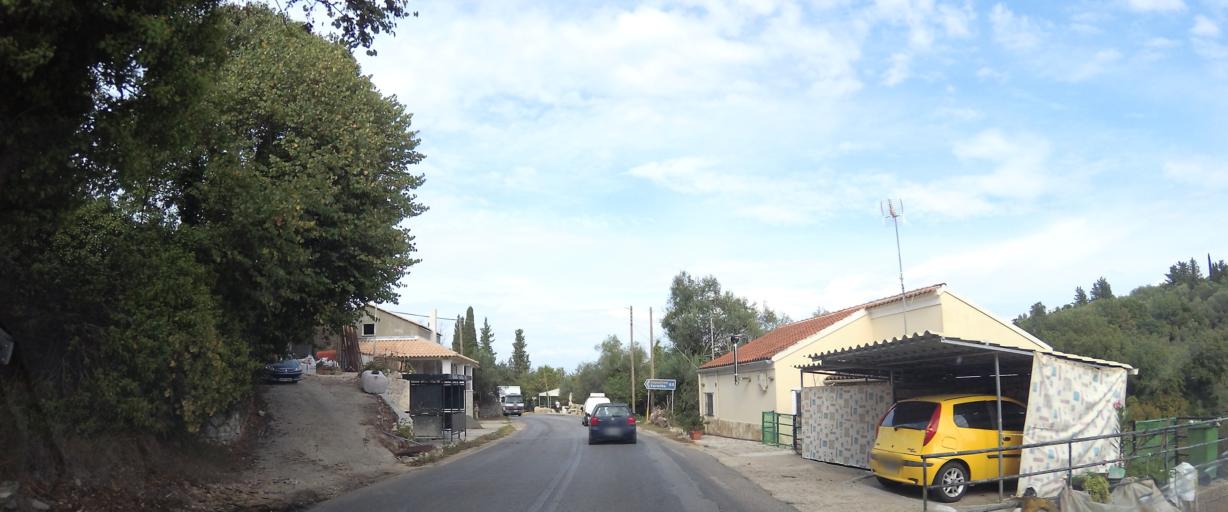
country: GR
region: Ionian Islands
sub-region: Nomos Kerkyras
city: Acharavi
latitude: 39.7669
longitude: 19.9331
